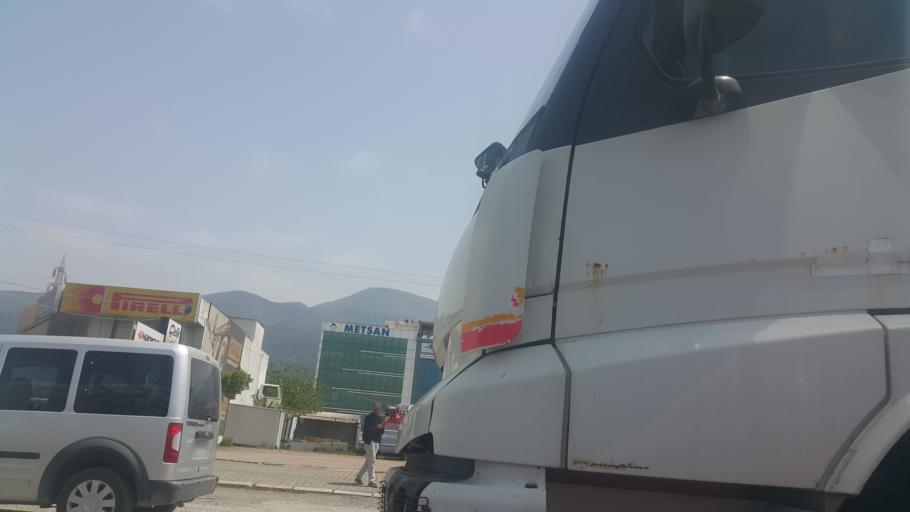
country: TR
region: Hatay
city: Yakacik
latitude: 36.7646
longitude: 36.2153
